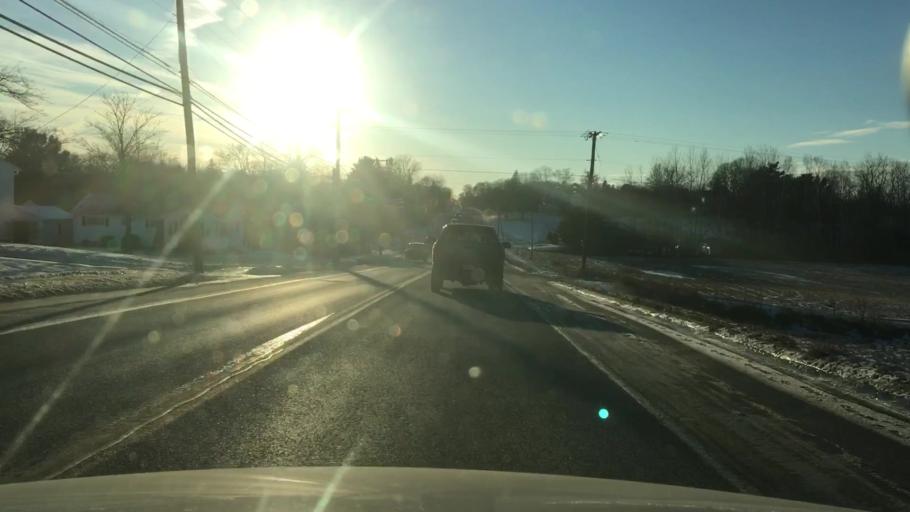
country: US
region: Maine
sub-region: Penobscot County
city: Brewer
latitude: 44.8029
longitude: -68.7480
